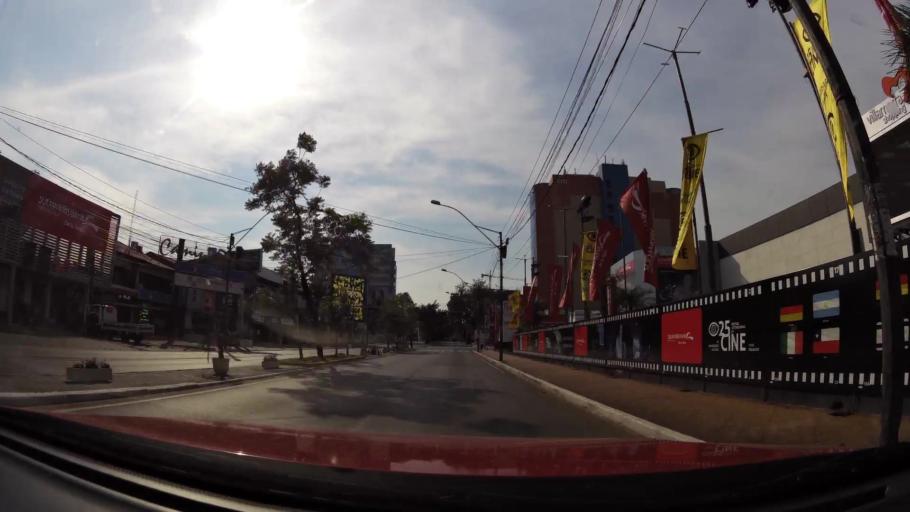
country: PY
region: Asuncion
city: Asuncion
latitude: -25.2941
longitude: -57.5803
